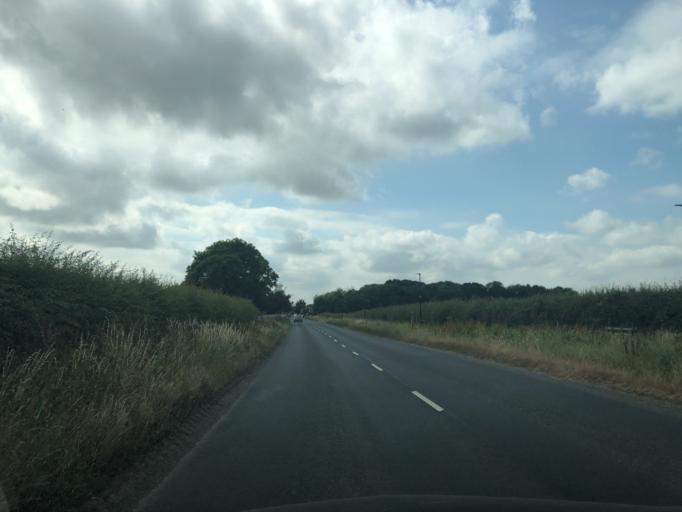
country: GB
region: England
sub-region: North Yorkshire
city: Stokesley
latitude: 54.4671
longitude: -1.2071
